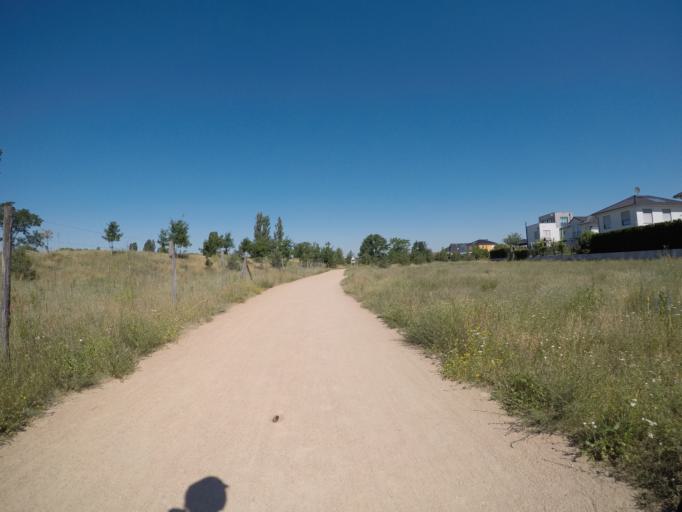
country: DE
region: Berlin
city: Karlshorst
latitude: 52.4718
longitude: 13.5326
